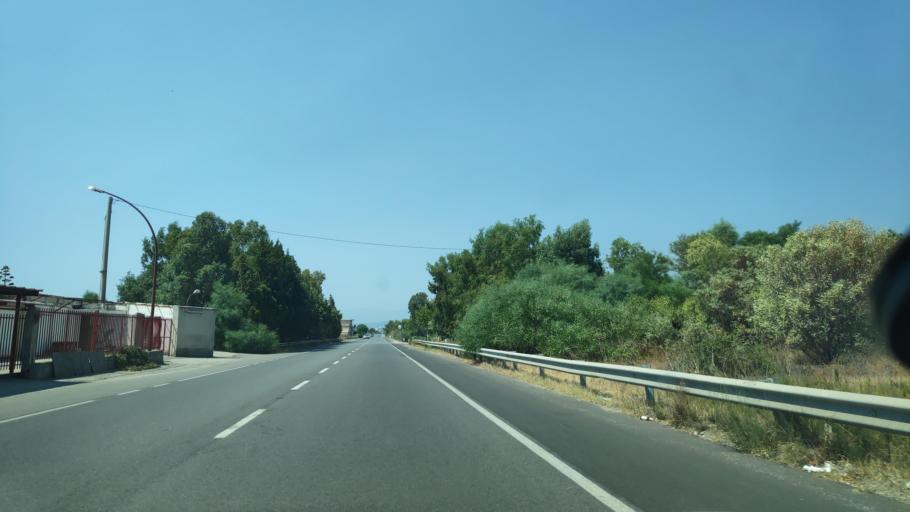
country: IT
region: Calabria
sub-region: Provincia di Reggio Calabria
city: Roccella Ionica
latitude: 38.3111
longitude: 16.3740
